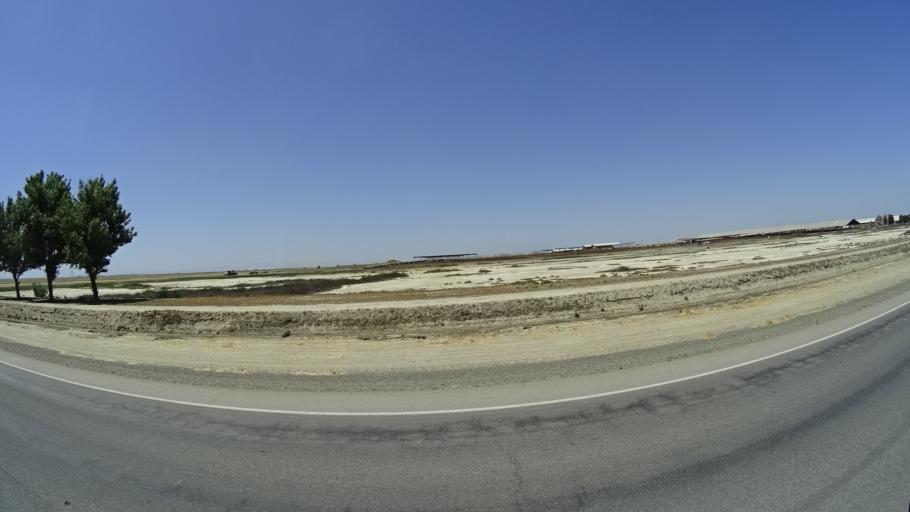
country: US
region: California
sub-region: Kings County
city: Home Garden
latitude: 36.1838
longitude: -119.6459
